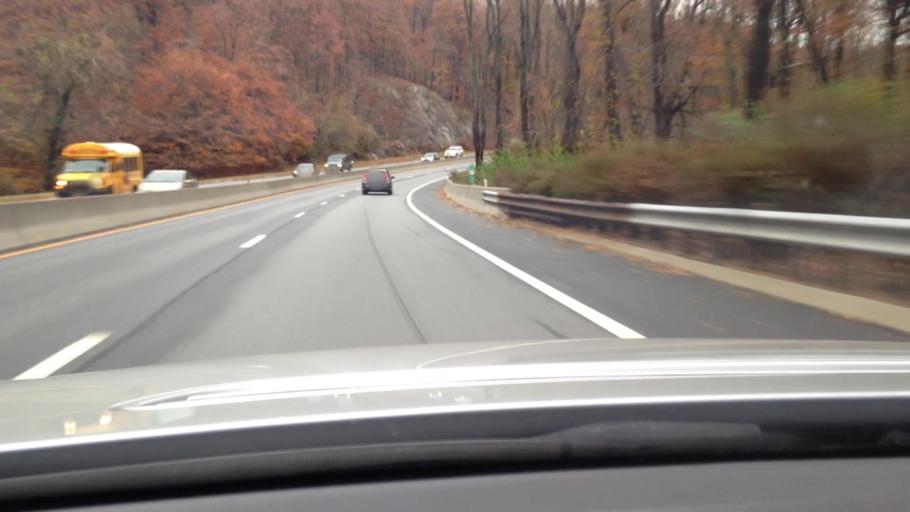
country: US
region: New York
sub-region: Westchester County
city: Elmsford
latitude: 41.0757
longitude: -73.8339
